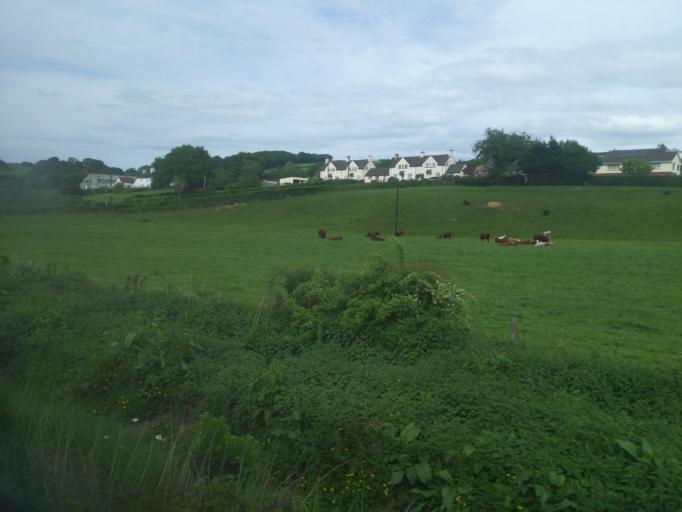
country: GB
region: England
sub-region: Devon
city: Barnstaple
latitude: 50.9916
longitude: -3.9839
